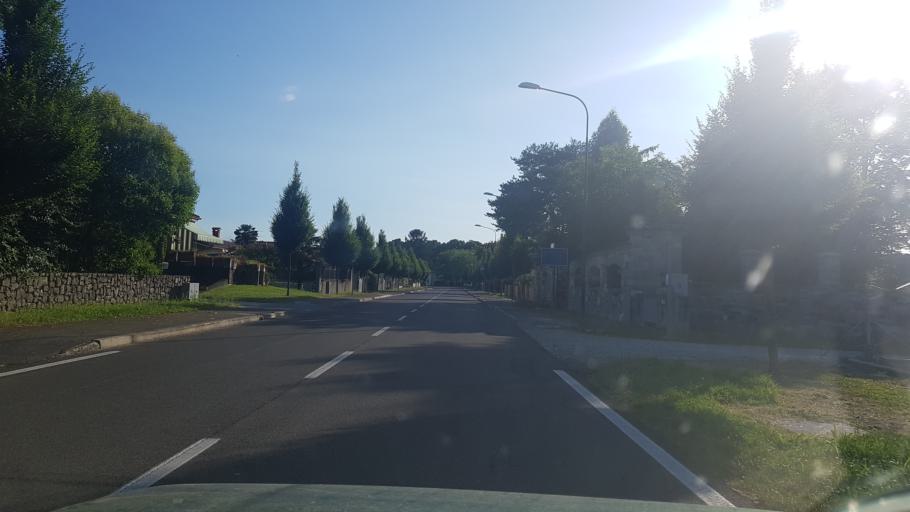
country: IT
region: Friuli Venezia Giulia
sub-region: Provincia di Gorizia
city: Moraro
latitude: 45.9340
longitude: 13.5018
